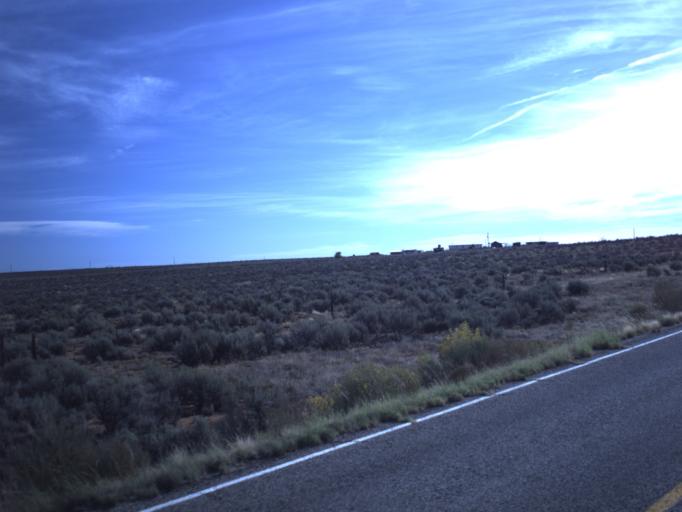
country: US
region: Utah
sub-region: San Juan County
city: Blanding
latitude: 37.4236
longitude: -109.3425
